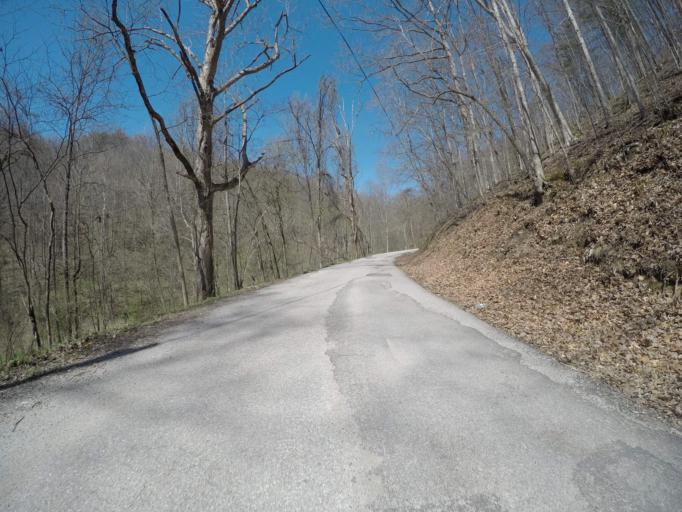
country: US
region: West Virginia
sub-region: Kanawha County
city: Charleston
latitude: 38.4105
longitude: -81.5881
